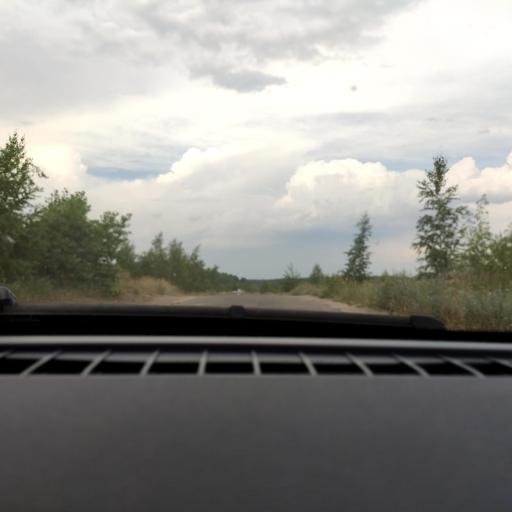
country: RU
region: Voronezj
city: Somovo
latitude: 51.7694
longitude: 39.3329
